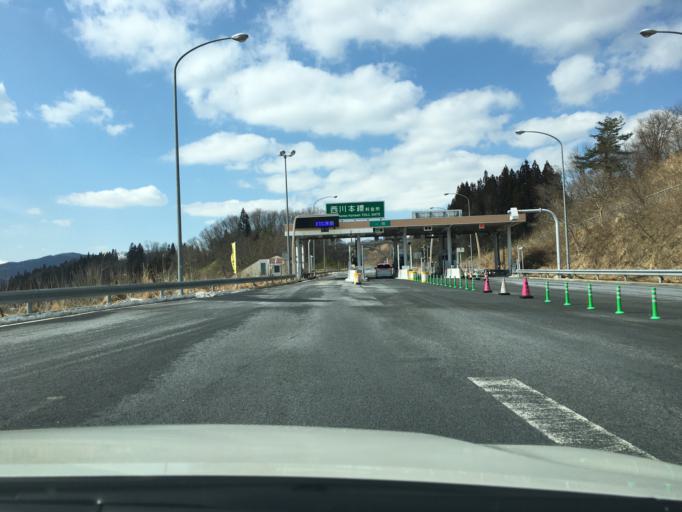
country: JP
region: Yamagata
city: Sagae
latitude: 38.4243
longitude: 140.1637
